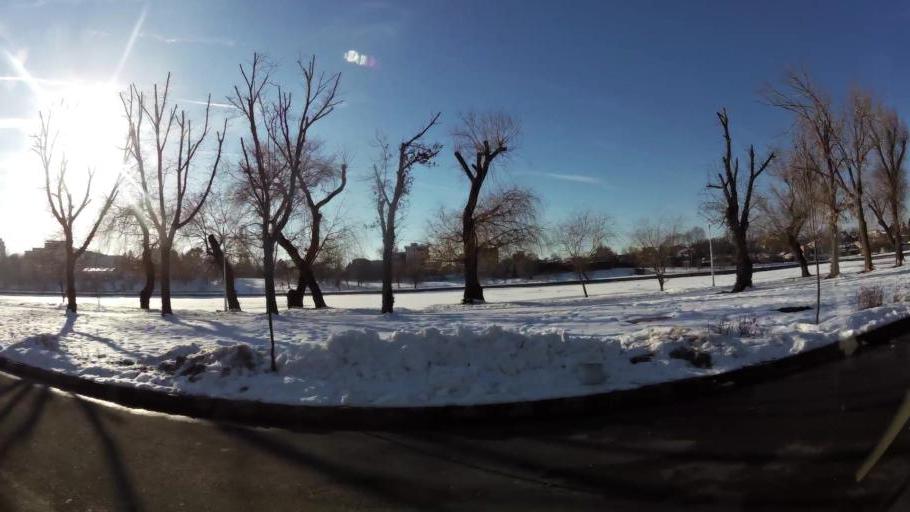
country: RO
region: Ilfov
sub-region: Comuna Fundeni-Dobroesti
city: Fundeni
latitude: 44.4687
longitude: 26.1310
